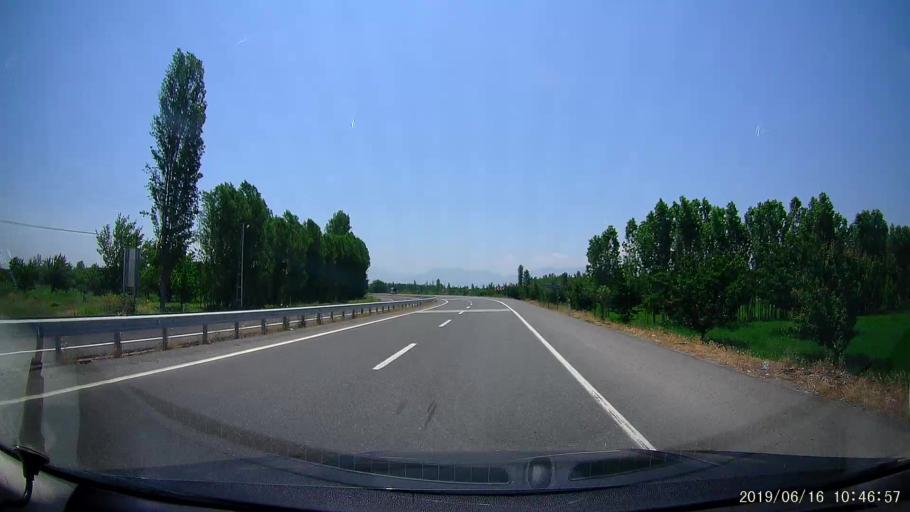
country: AM
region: Armavir
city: Shenavan
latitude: 40.0165
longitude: 43.8827
